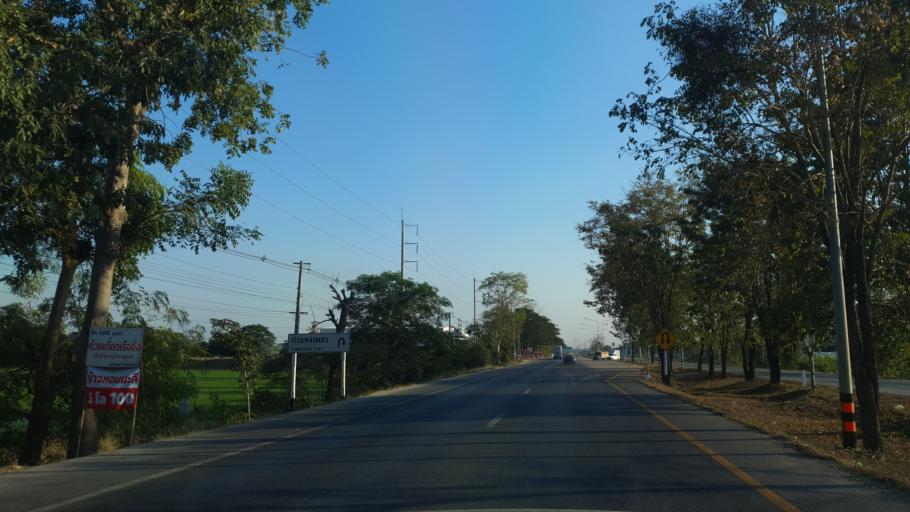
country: TH
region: Kamphaeng Phet
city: Khlong Khlung
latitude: 16.2227
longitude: 99.6998
